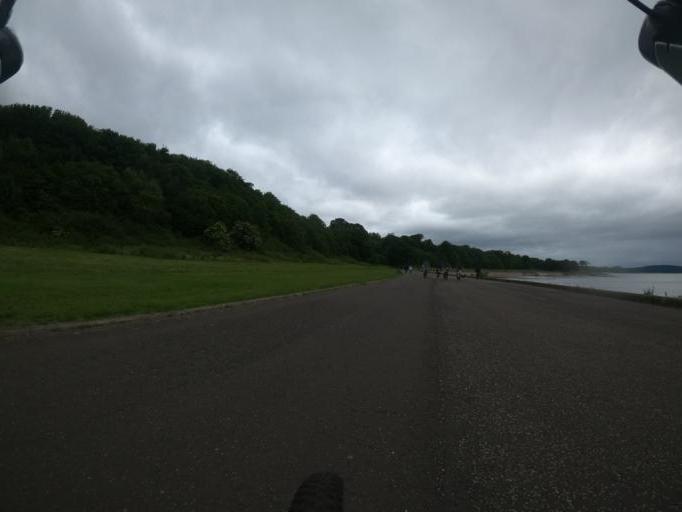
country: GB
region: Scotland
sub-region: Edinburgh
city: Edinburgh
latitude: 55.9800
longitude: -3.2599
